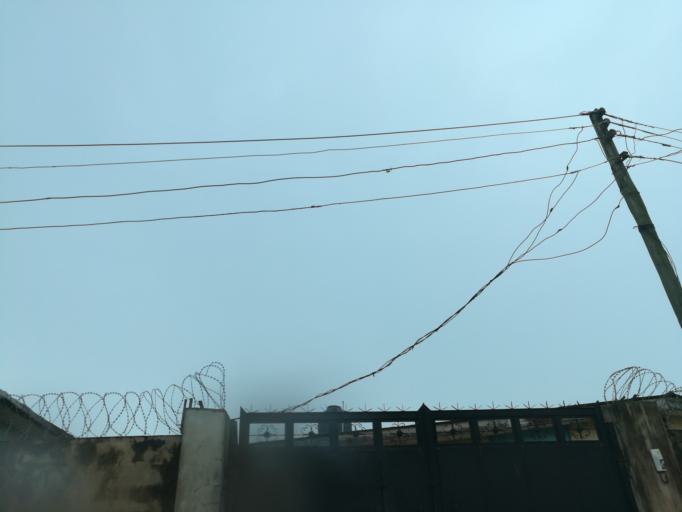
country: NG
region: Lagos
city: Oshodi
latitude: 6.5589
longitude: 3.3372
